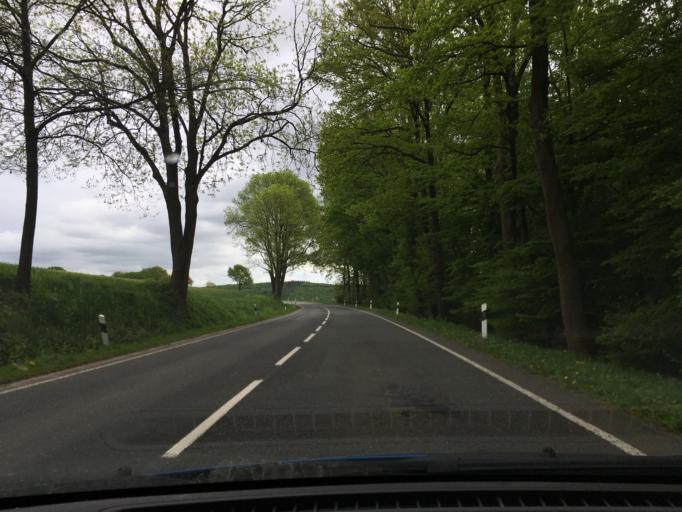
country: DE
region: Lower Saxony
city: Bodenfelde
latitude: 51.6843
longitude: 9.5097
